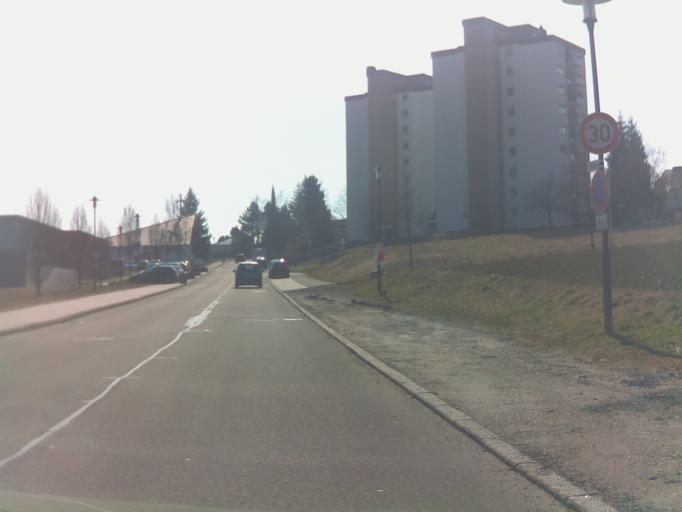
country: DE
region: Baden-Wuerttemberg
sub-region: Karlsruhe Region
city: Horb am Neckar
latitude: 48.4524
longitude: 8.6874
